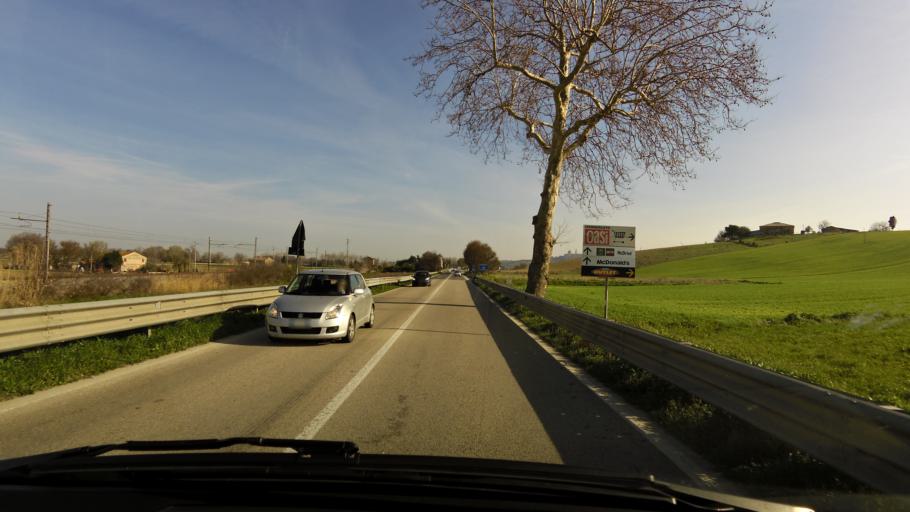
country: IT
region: The Marches
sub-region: Provincia di Ancona
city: Villa Musone
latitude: 43.4689
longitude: 13.6000
